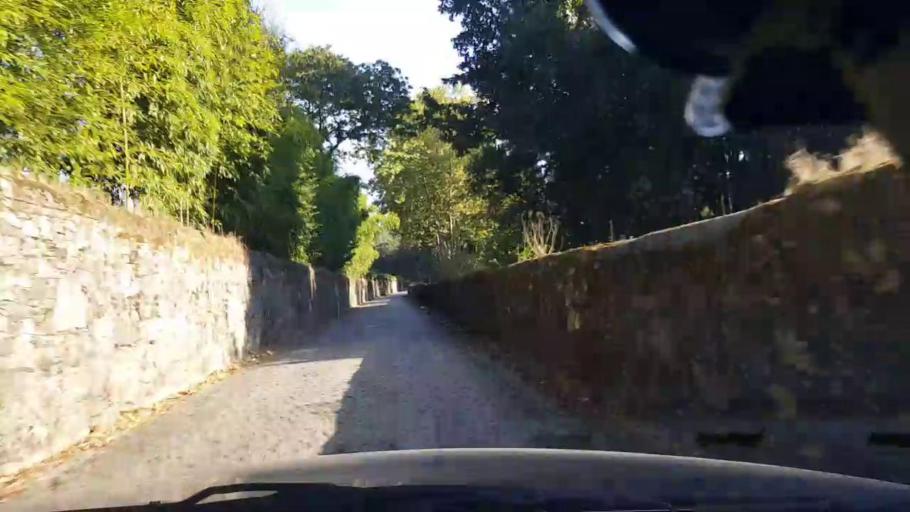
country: PT
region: Porto
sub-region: Vila do Conde
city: Arvore
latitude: 41.3431
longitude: -8.6875
